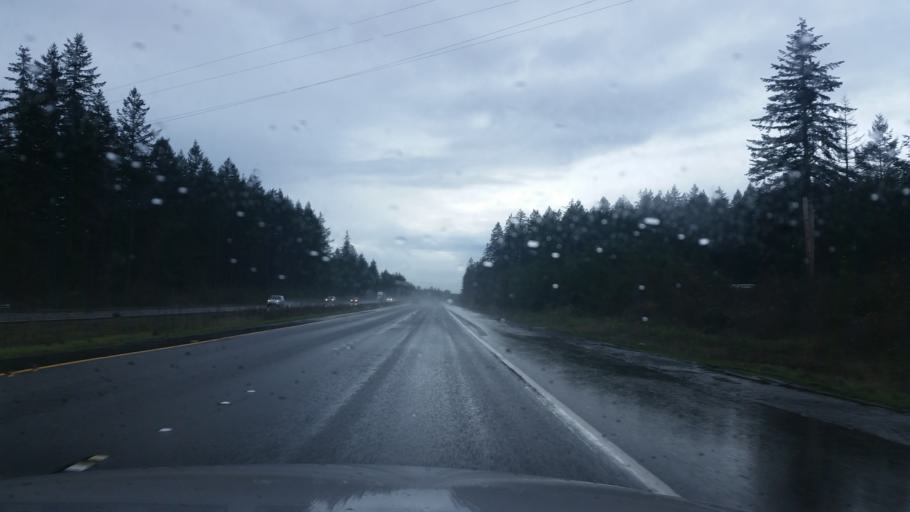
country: US
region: Washington
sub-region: King County
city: Maple Valley
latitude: 47.3849
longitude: -122.0641
